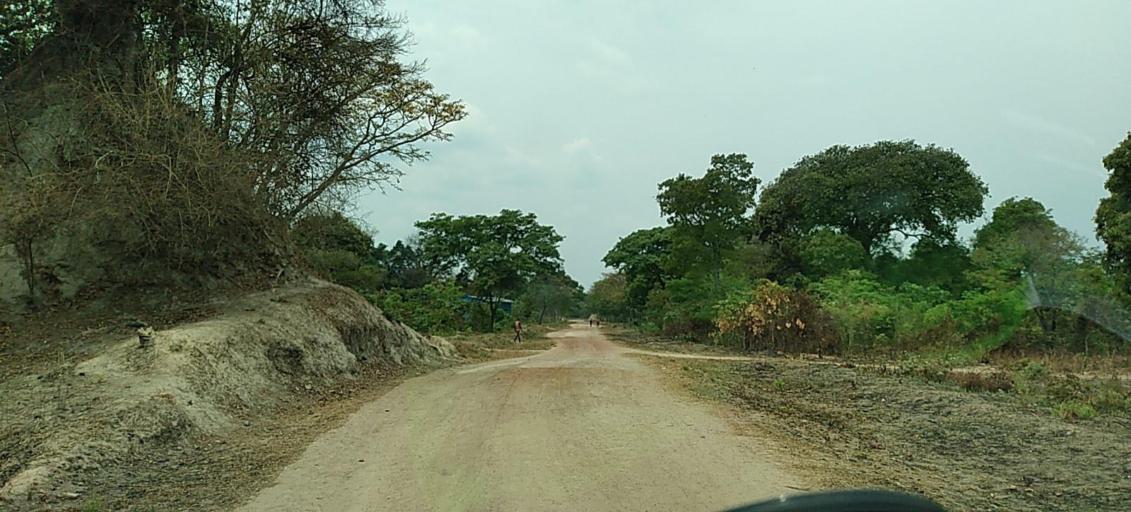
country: ZM
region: North-Western
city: Solwezi
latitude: -12.7850
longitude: 26.5153
